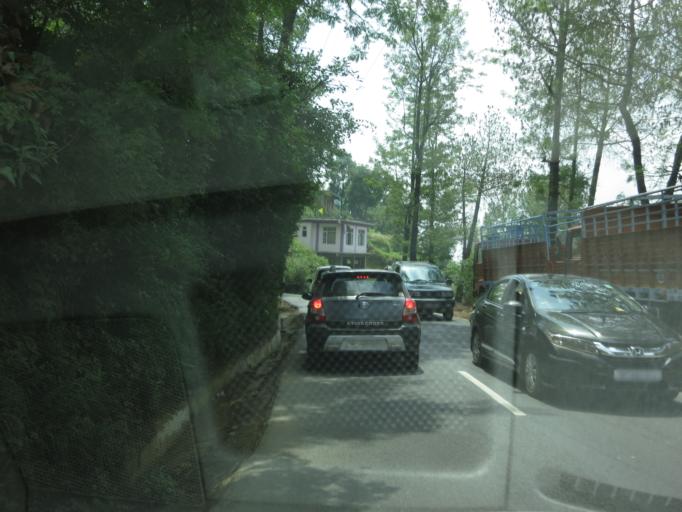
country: IN
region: Himachal Pradesh
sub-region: Solan
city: Dagshai
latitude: 30.8985
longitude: 77.0682
